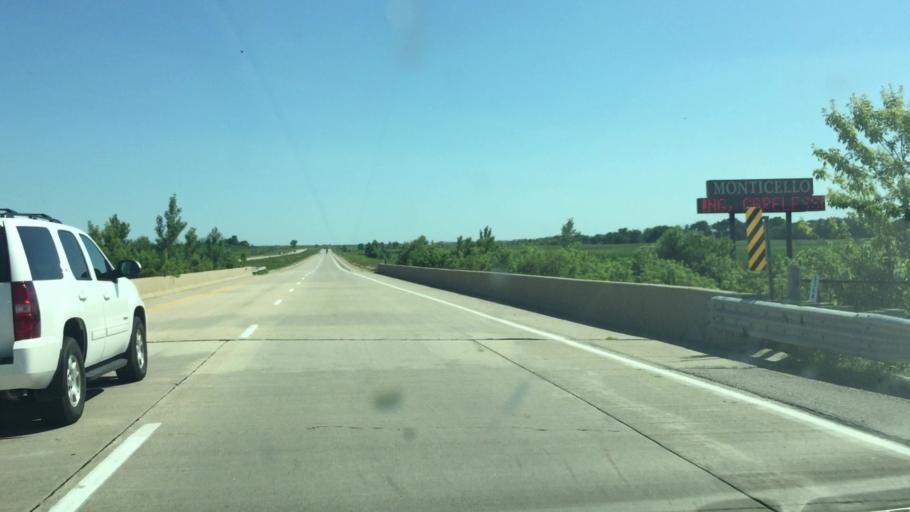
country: US
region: Iowa
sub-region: Jones County
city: Monticello
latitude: 42.2239
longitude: -91.1724
